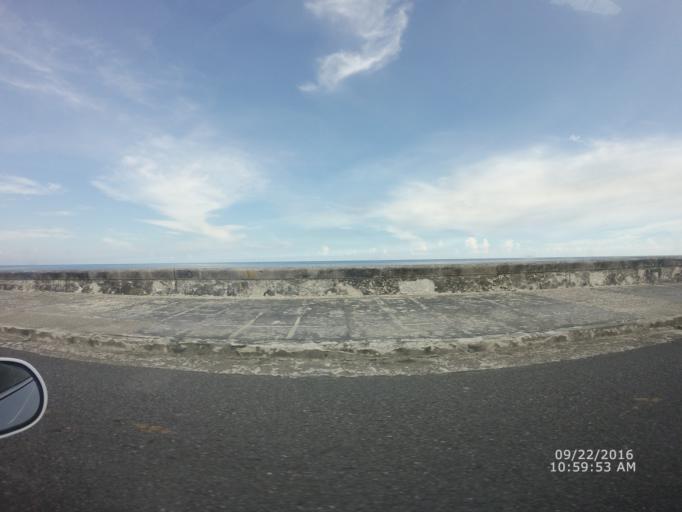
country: CU
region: La Habana
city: Havana
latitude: 23.1460
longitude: -82.3937
